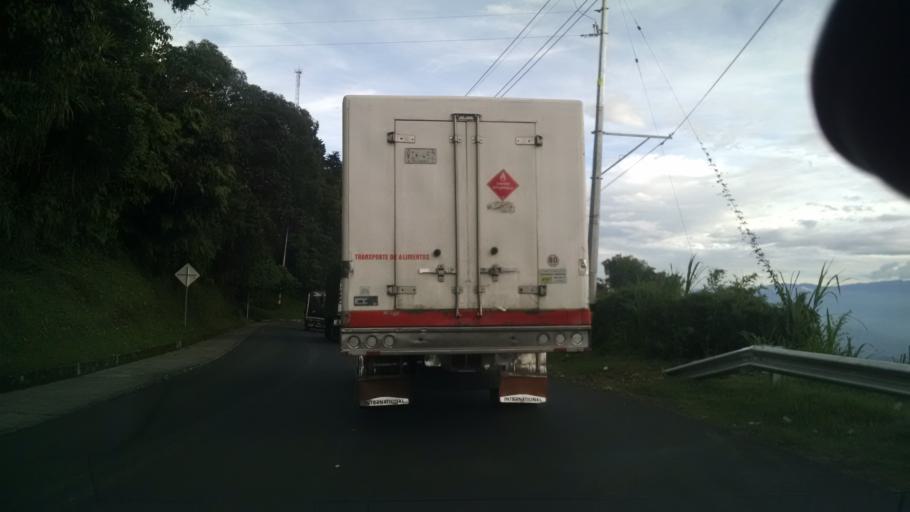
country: CO
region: Antioquia
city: Santa Barbara
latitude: 5.9192
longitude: -75.5787
